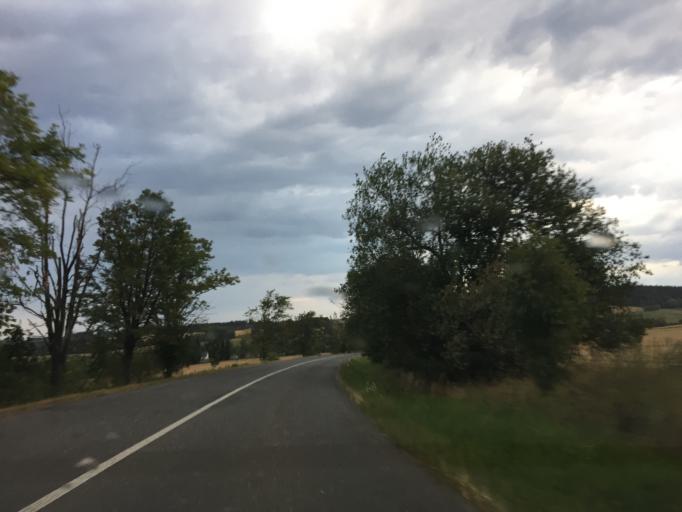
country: CZ
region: Liberecky
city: Mala Skala
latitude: 50.6752
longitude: 15.1834
